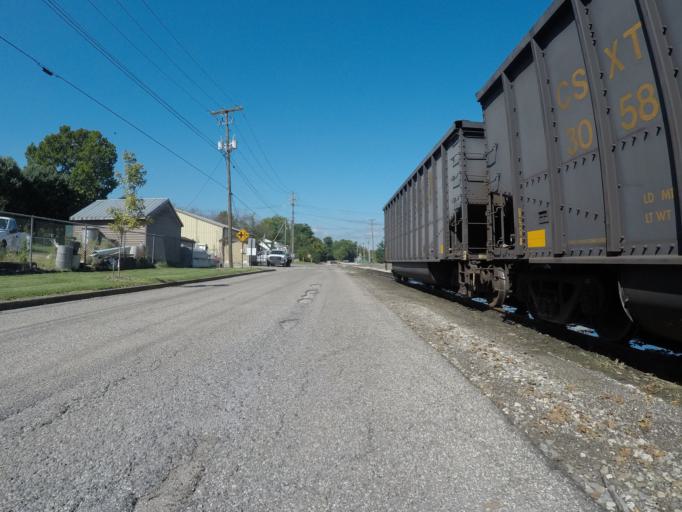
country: US
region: West Virginia
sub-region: Wayne County
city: Ceredo
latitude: 38.3984
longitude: -82.5574
